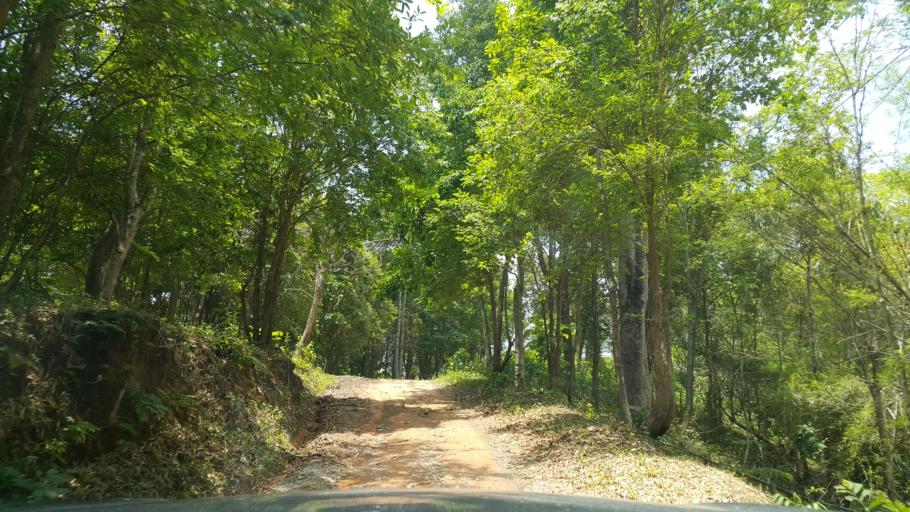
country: TH
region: Chiang Rai
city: Chiang Rai
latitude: 20.0010
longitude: 99.7013
